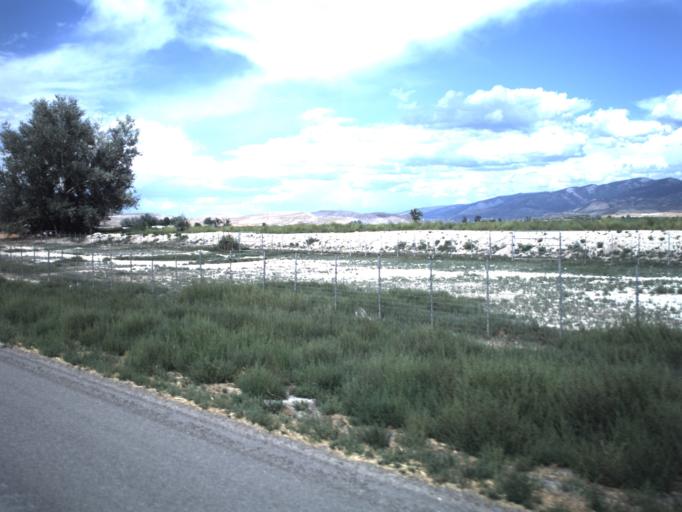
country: US
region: Utah
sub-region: Sanpete County
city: Centerfield
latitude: 39.0992
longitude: -111.8198
